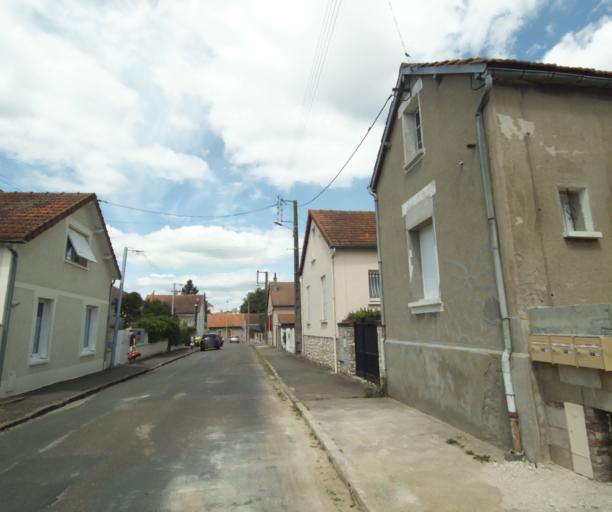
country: FR
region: Centre
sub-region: Departement d'Eure-et-Loir
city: Luce
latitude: 48.4380
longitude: 1.4580
